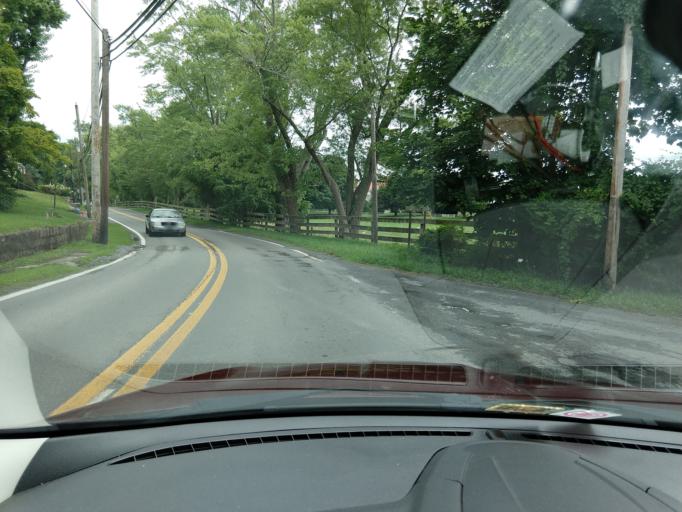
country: US
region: West Virginia
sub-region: Fayette County
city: Oak Hill
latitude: 37.9712
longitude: -81.1519
